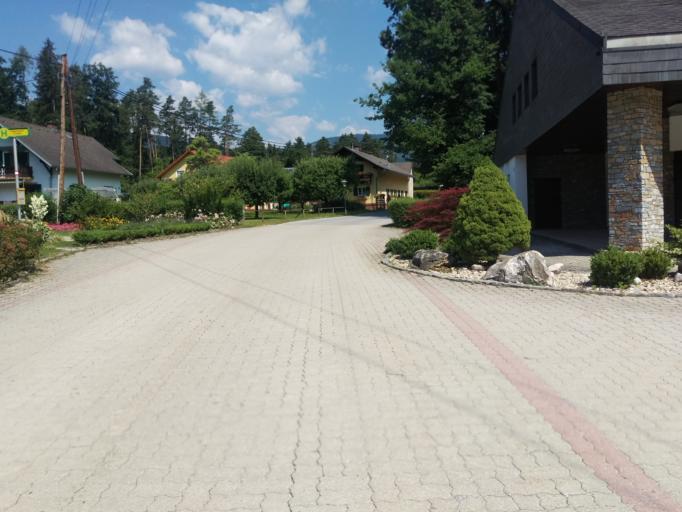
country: AT
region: Styria
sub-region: Politischer Bezirk Graz-Umgebung
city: Sankt Radegund bei Graz
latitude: 47.1402
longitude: 15.4903
